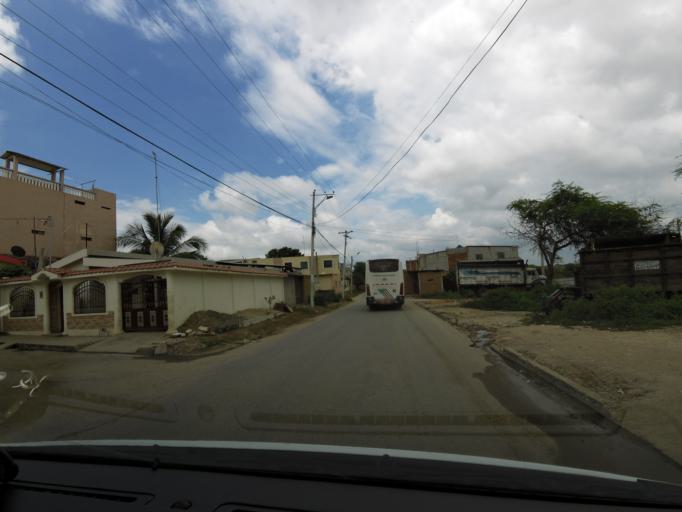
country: EC
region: El Oro
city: Huaquillas
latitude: -3.4838
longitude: -80.2270
